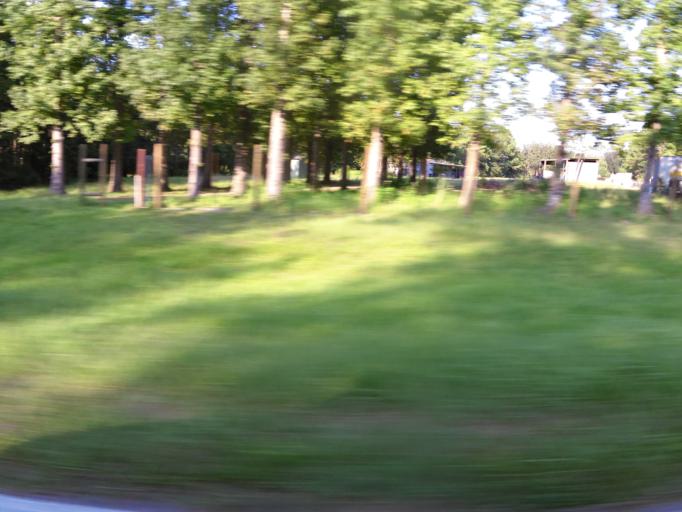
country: US
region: Florida
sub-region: Duval County
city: Baldwin
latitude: 30.3639
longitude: -82.0114
